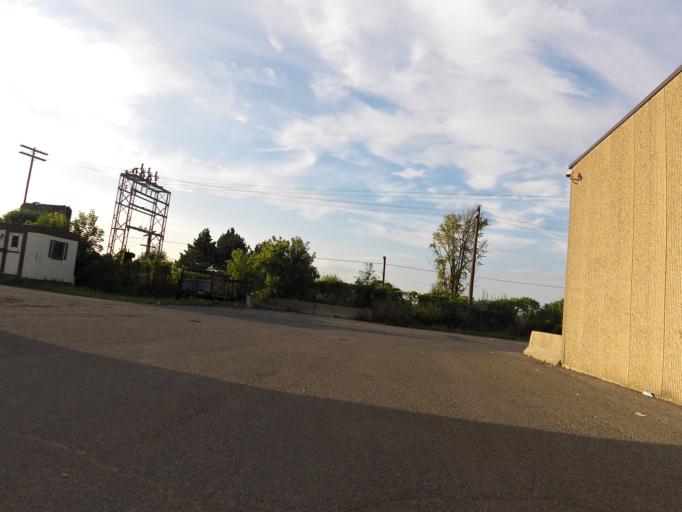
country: CA
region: Ontario
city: Bells Corners
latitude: 45.3305
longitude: -75.8144
